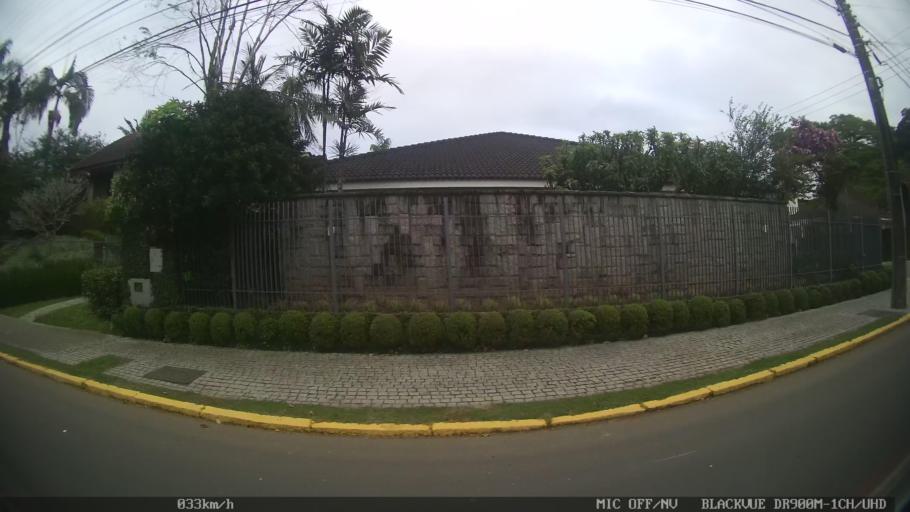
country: BR
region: Santa Catarina
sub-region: Joinville
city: Joinville
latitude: -26.2901
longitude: -48.8537
